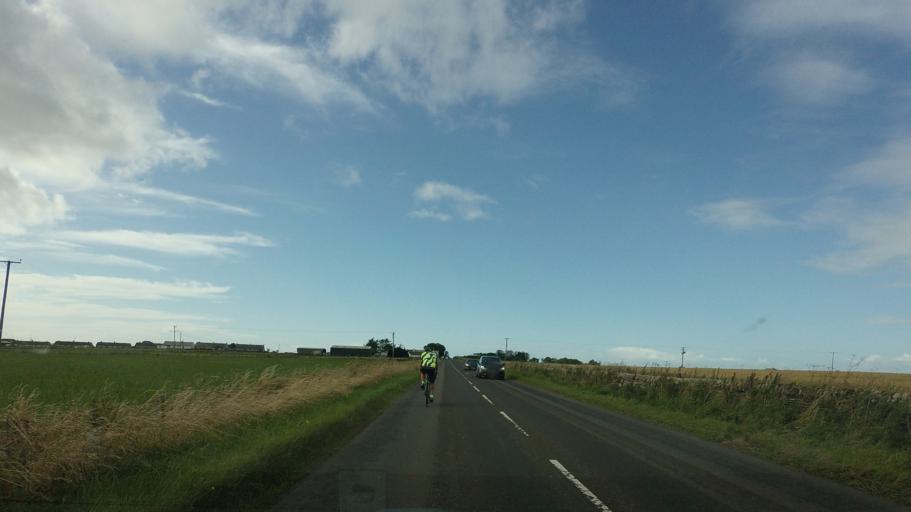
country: GB
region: Scotland
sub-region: Highland
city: Wick
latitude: 58.4737
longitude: -3.1385
